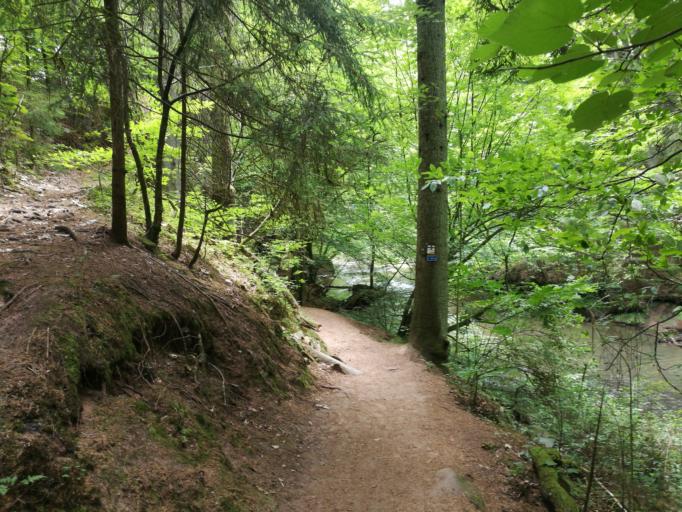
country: DE
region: Bavaria
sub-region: Regierungsbezirk Mittelfranken
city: Schwarzenbruck
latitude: 49.3511
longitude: 11.2238
